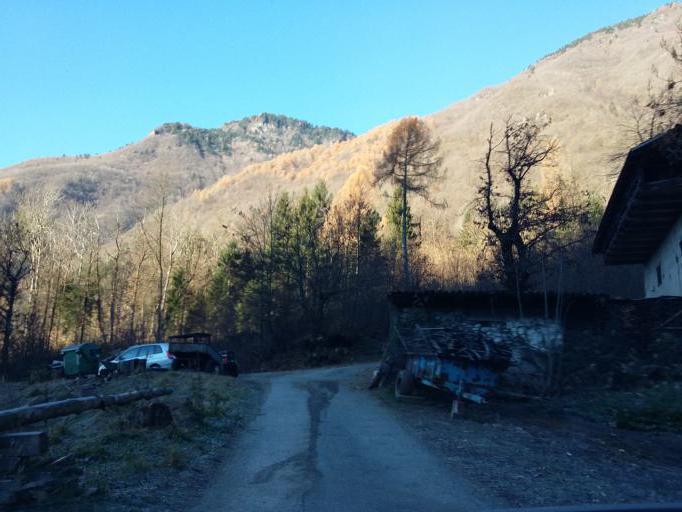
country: IT
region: Trentino-Alto Adige
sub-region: Provincia di Trento
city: Storo
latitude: 45.8664
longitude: 10.5751
